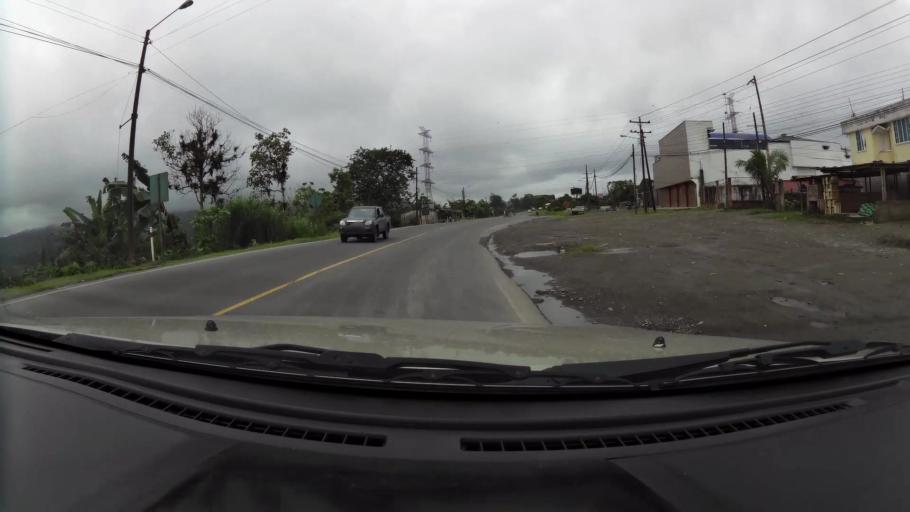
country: EC
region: Santo Domingo de los Tsachilas
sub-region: Canton Santo Domingo de los Colorados
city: Santo Domingo de los Colorados
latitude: -0.2585
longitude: -79.1230
